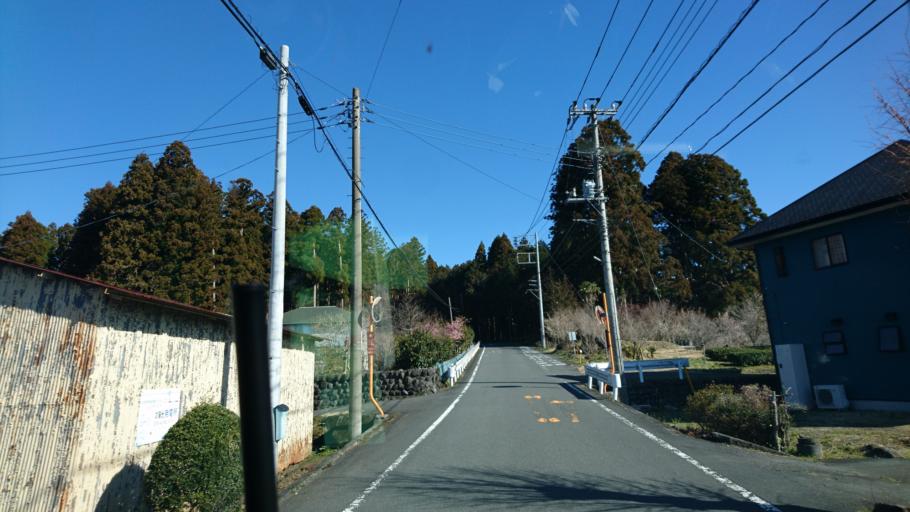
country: JP
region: Shizuoka
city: Fujinomiya
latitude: 35.3299
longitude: 138.5753
